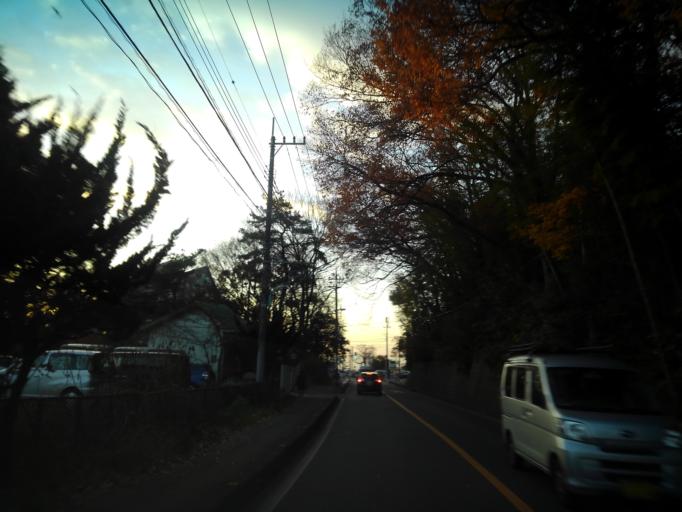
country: JP
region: Tokyo
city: Higashimurayama-shi
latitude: 35.7705
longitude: 139.4380
